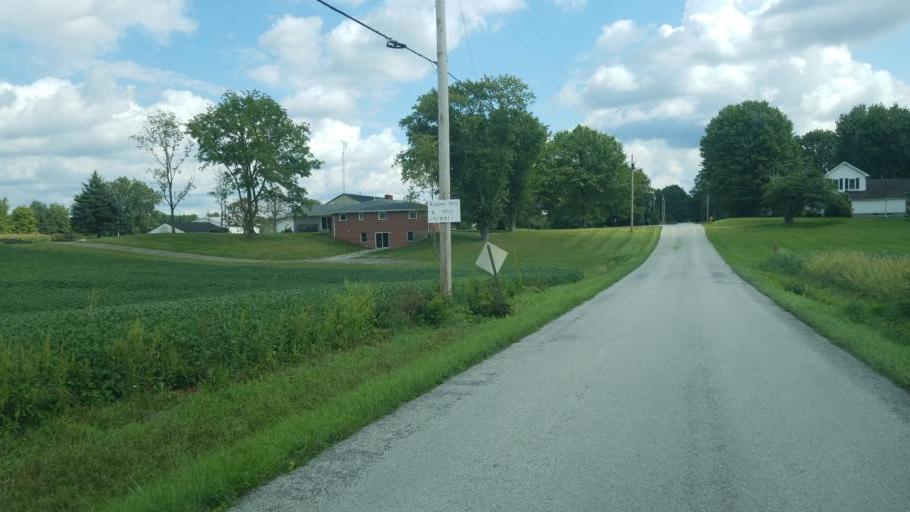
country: US
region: Ohio
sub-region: Huron County
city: Monroeville
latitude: 41.1676
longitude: -82.6629
